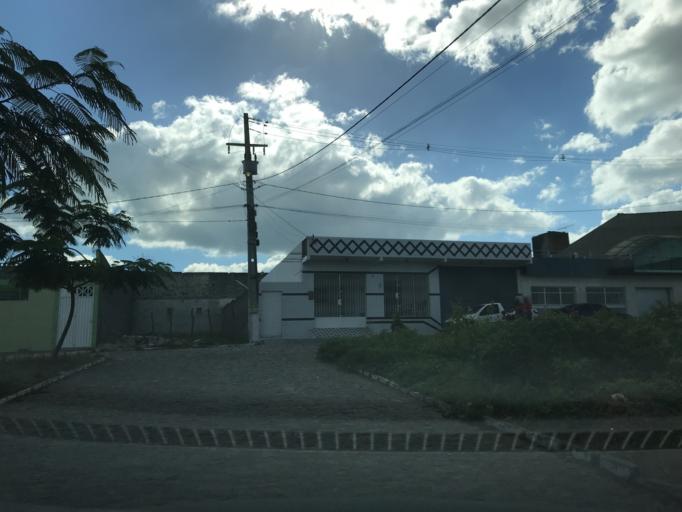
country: BR
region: Pernambuco
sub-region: Bezerros
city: Bezerros
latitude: -8.2323
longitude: -35.7555
